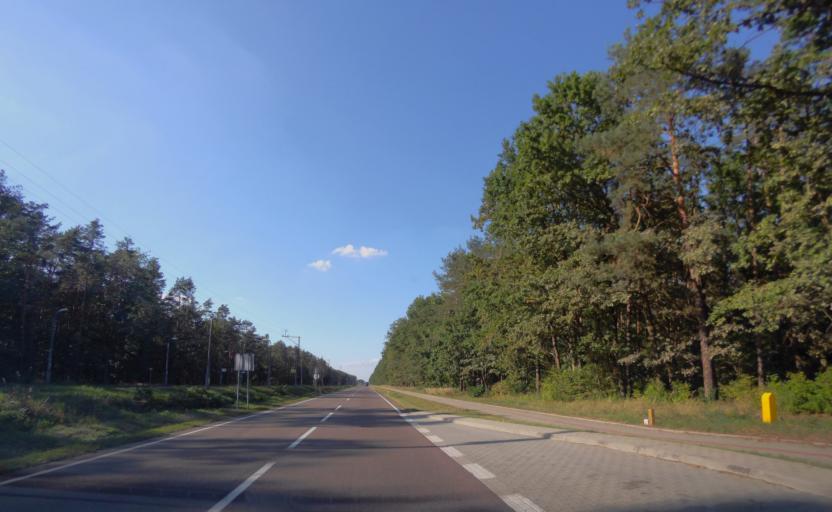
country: PL
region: Subcarpathian Voivodeship
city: Nowa Sarzyna
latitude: 50.3045
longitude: 22.3647
